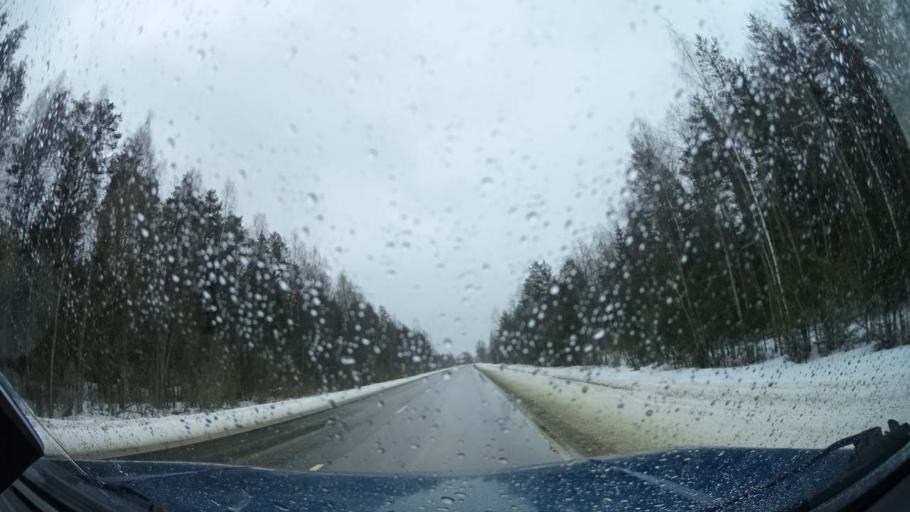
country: RU
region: Tverskaya
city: Gorodnya
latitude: 56.8504
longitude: 36.4123
